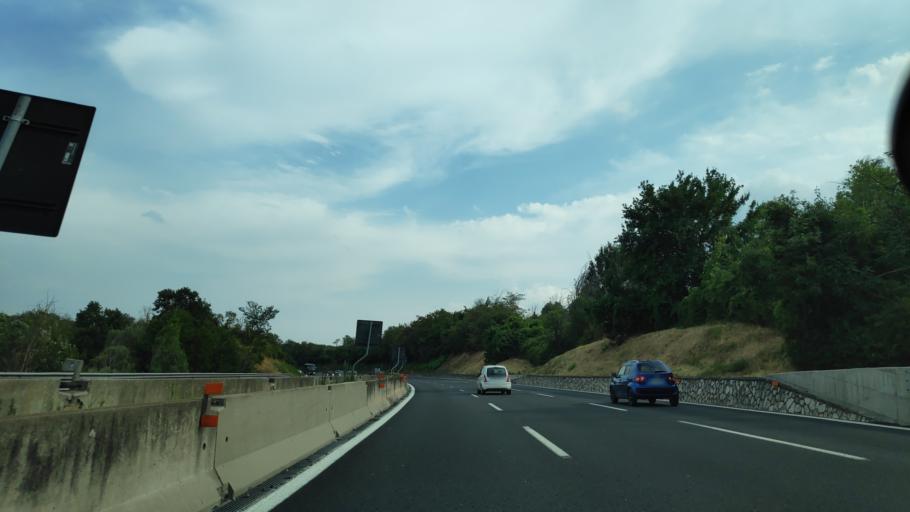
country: IT
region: Latium
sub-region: Citta metropolitana di Roma Capitale
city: Fiano Romano
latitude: 42.1809
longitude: 12.6022
